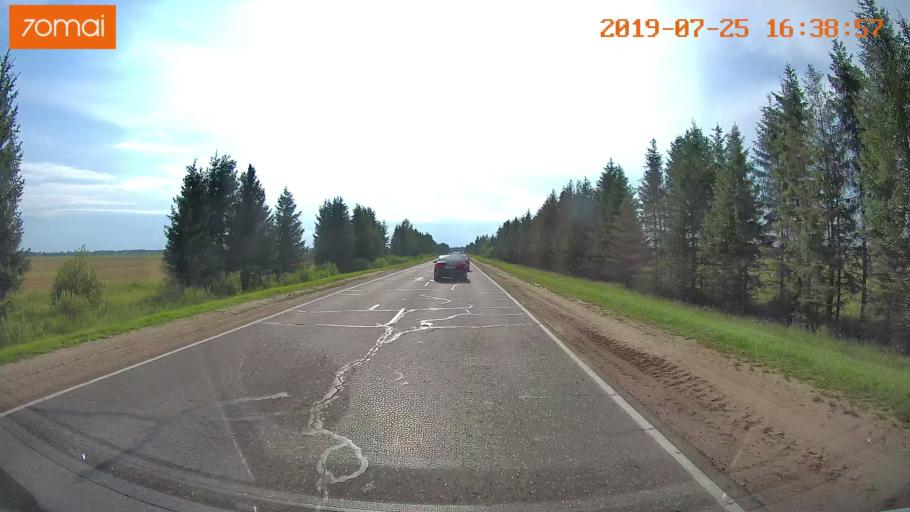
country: RU
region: Ivanovo
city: Privolzhsk
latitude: 57.3873
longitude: 41.3374
